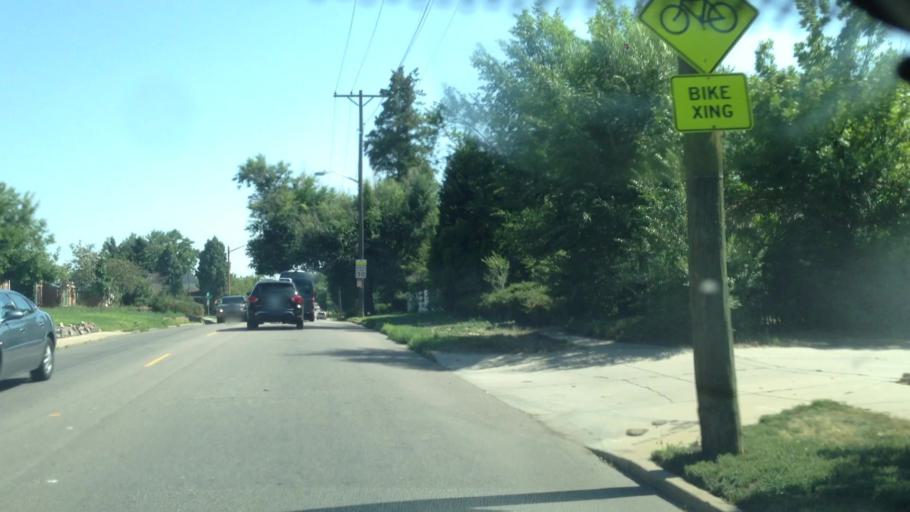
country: US
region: Colorado
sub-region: Arapahoe County
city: Glendale
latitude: 39.7367
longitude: -104.9035
